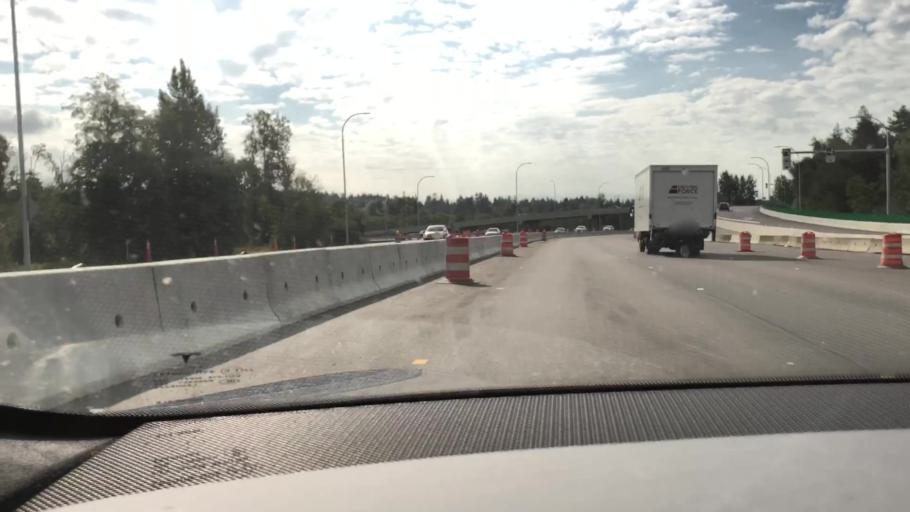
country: CA
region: British Columbia
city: Delta
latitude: 49.1356
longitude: -122.9302
